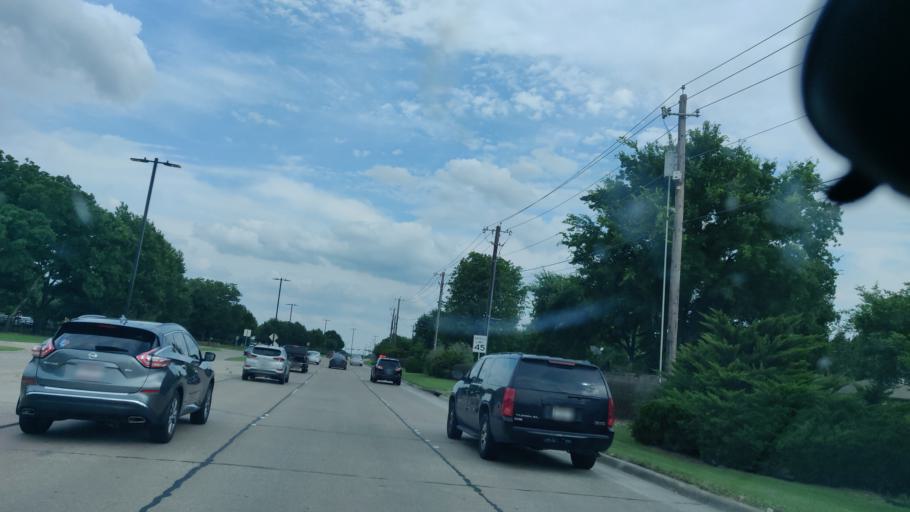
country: US
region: Texas
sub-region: Dallas County
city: Sachse
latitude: 32.9368
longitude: -96.6024
